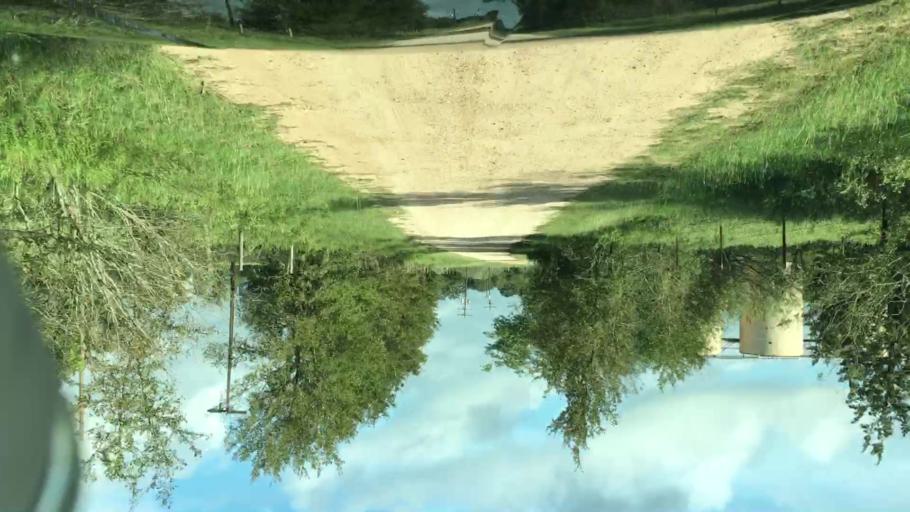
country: US
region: Texas
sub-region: Burleson County
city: Somerville
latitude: 30.3037
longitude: -96.7301
